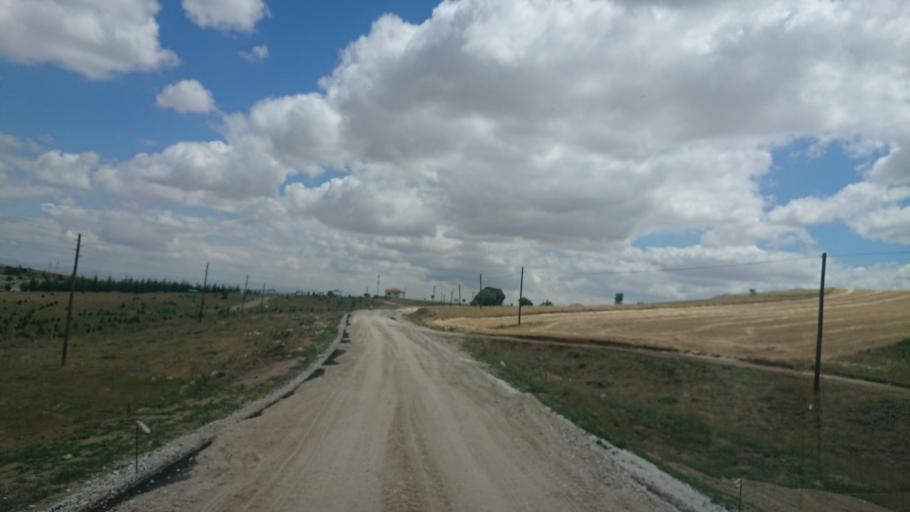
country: TR
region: Aksaray
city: Agacoren
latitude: 38.8617
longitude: 33.9488
